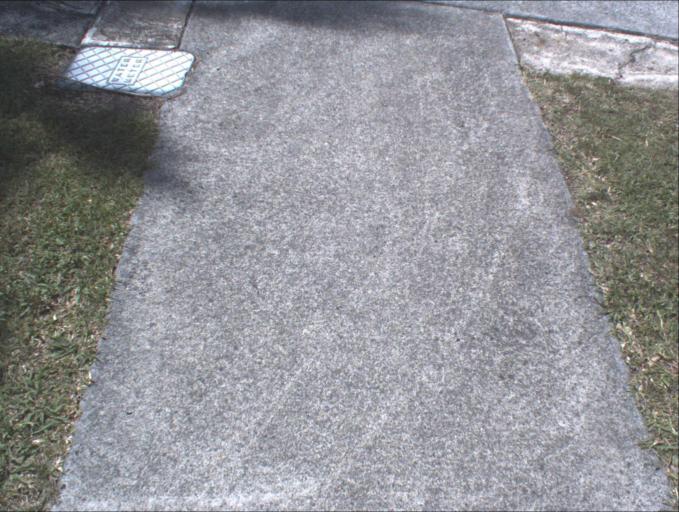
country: AU
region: Queensland
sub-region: Logan
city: Slacks Creek
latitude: -27.6682
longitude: 153.1437
